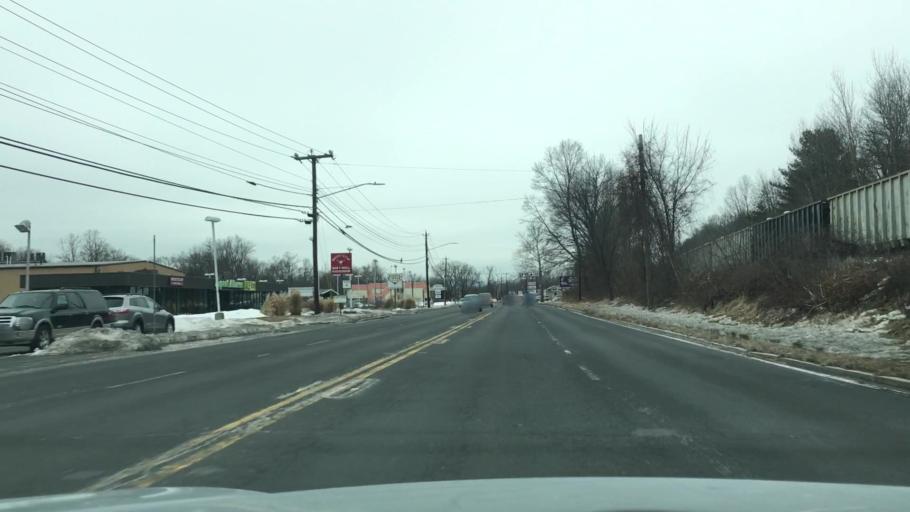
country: US
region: Massachusetts
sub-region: Hampden County
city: Westfield
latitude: 42.1098
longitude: -72.7085
